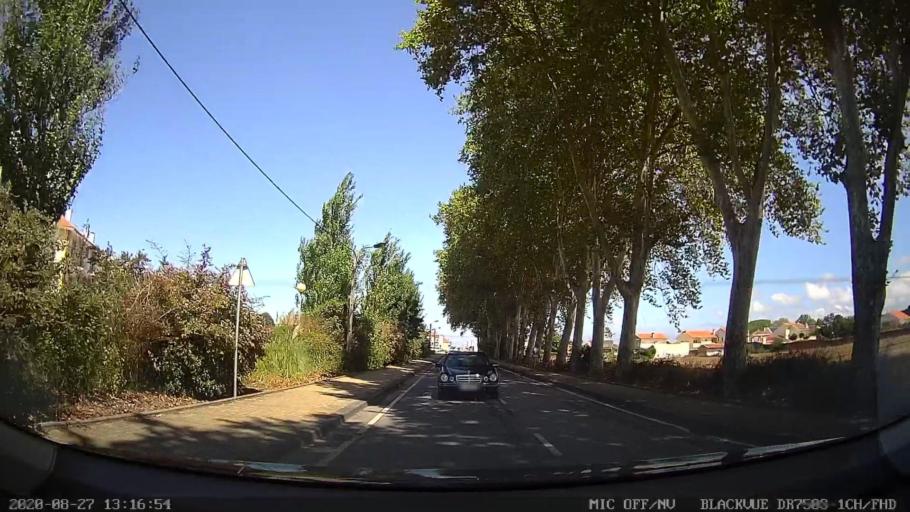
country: PT
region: Aveiro
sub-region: Ilhavo
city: Ilhavo
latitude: 40.5853
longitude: -8.6793
